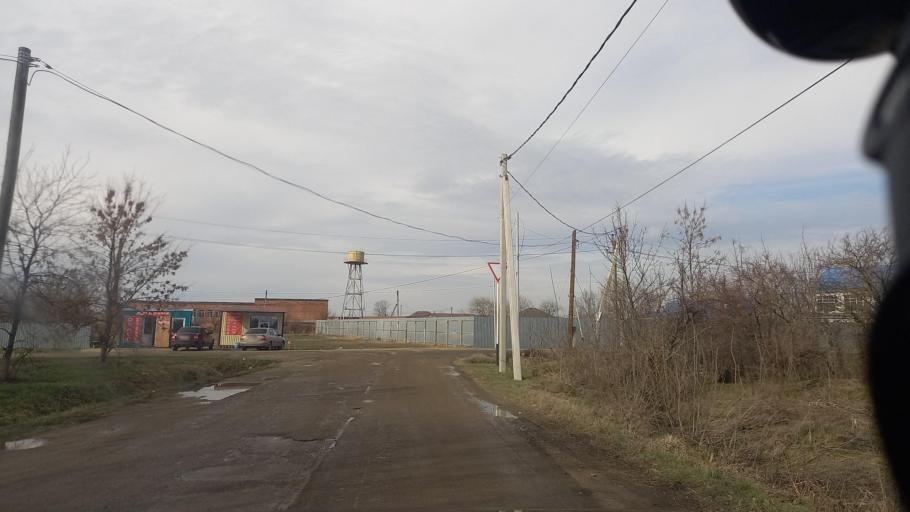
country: RU
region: Adygeya
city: Takhtamukay
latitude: 44.9171
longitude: 39.0037
